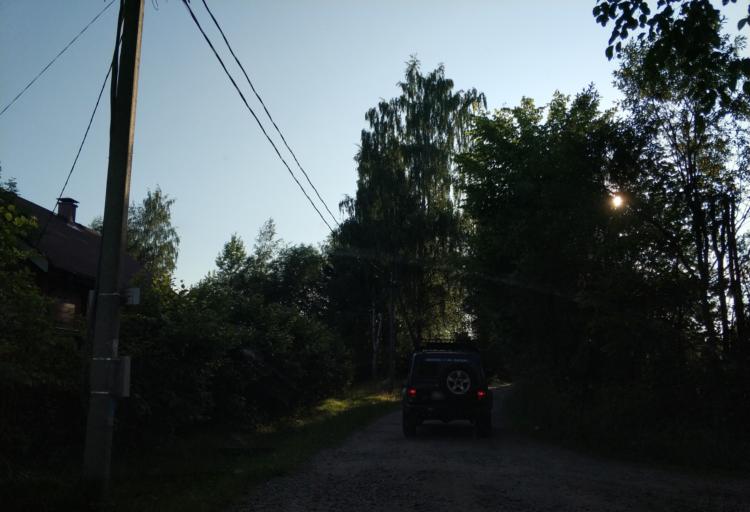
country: RU
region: Leningrad
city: Sapernoye
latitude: 60.6950
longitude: 29.9830
